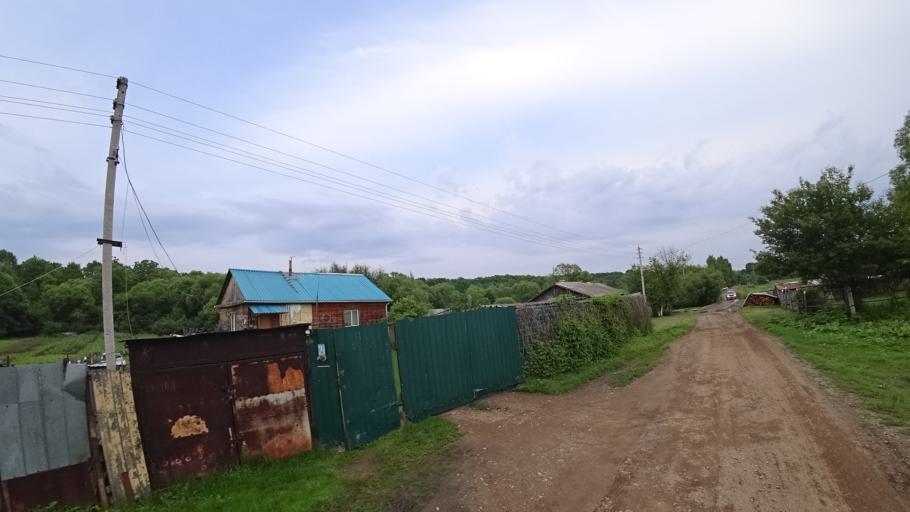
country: RU
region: Primorskiy
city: Novosysoyevka
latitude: 44.2371
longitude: 133.3793
